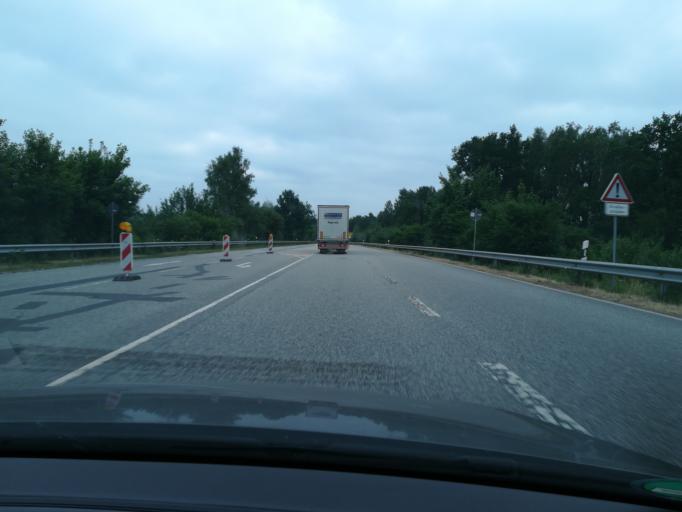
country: DE
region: Schleswig-Holstein
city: Kasseburg
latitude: 53.5590
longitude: 10.4103
